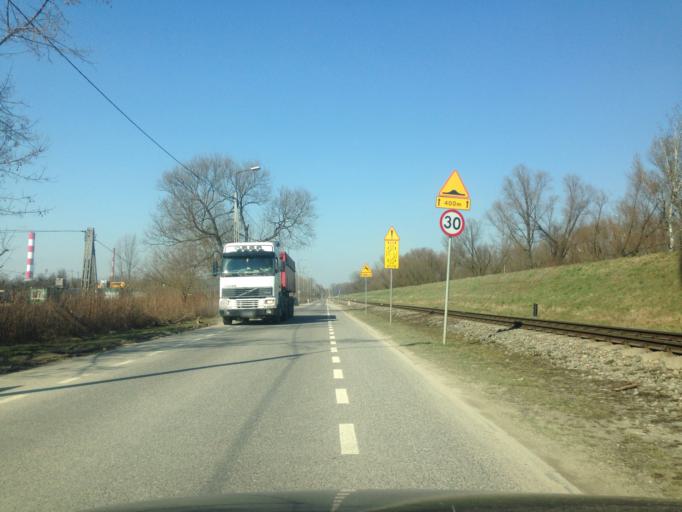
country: PL
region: Masovian Voivodeship
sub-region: Warszawa
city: Wilanow
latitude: 52.1764
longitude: 21.1169
